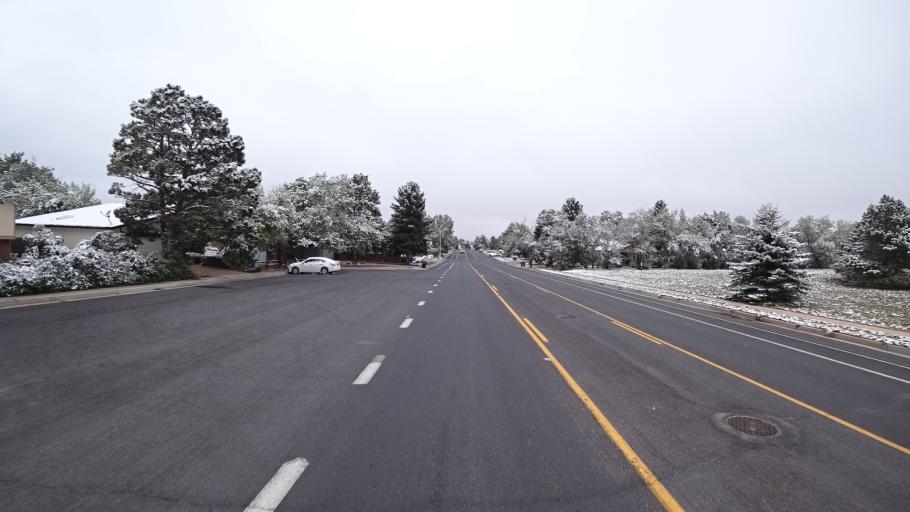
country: US
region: Colorado
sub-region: El Paso County
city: Cimarron Hills
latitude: 38.9176
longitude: -104.7648
